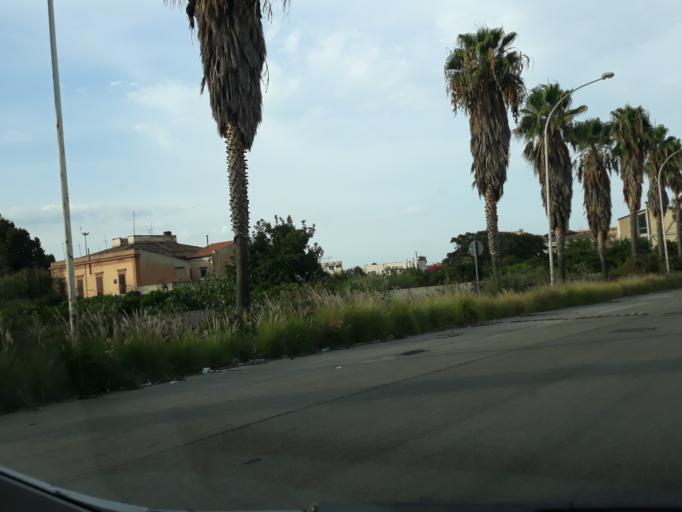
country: IT
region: Sicily
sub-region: Palermo
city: Ciaculli
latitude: 38.0902
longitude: 13.4064
